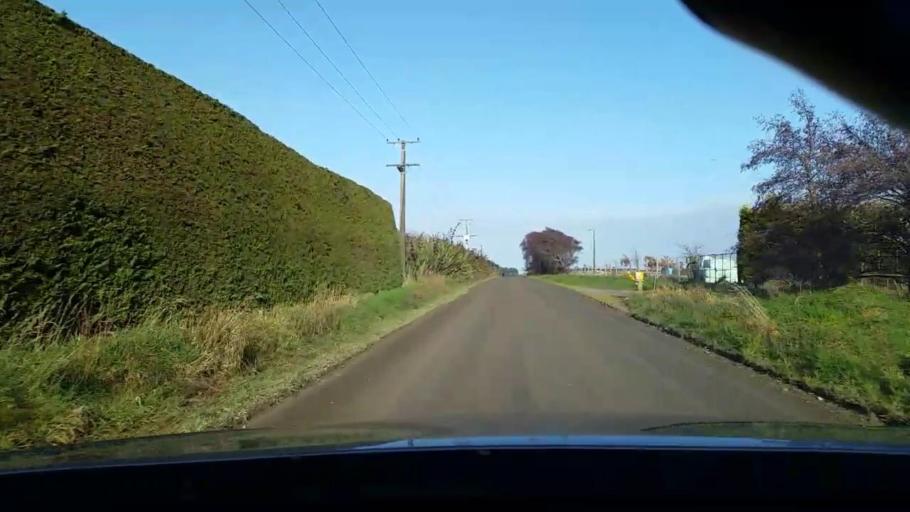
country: NZ
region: Southland
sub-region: Invercargill City
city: Invercargill
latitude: -46.3018
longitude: 168.3033
